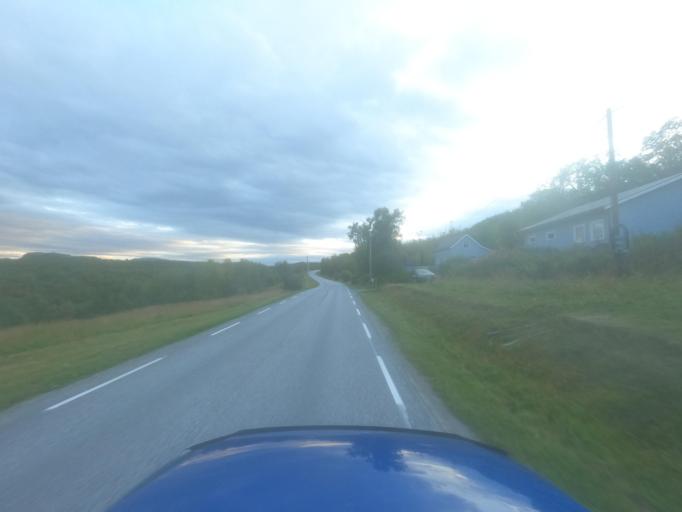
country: NO
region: Finnmark Fylke
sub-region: Porsanger
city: Lakselv
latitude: 70.2188
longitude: 24.9262
